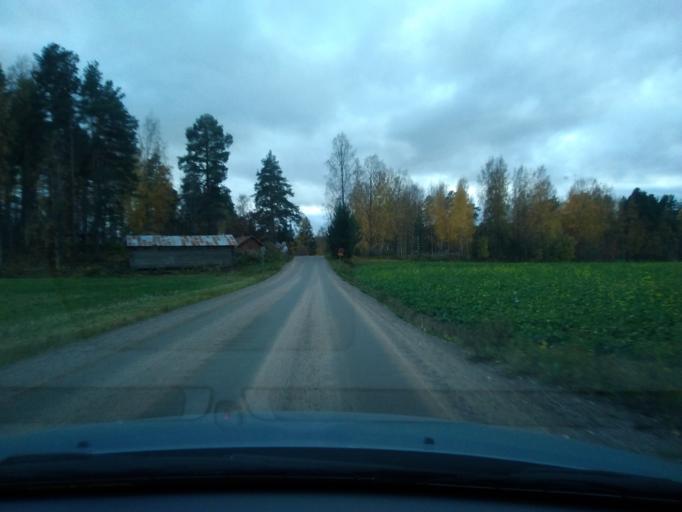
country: FI
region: Central Finland
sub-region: Saarijaervi-Viitasaari
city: Saarijaervi
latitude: 62.6919
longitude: 25.3184
